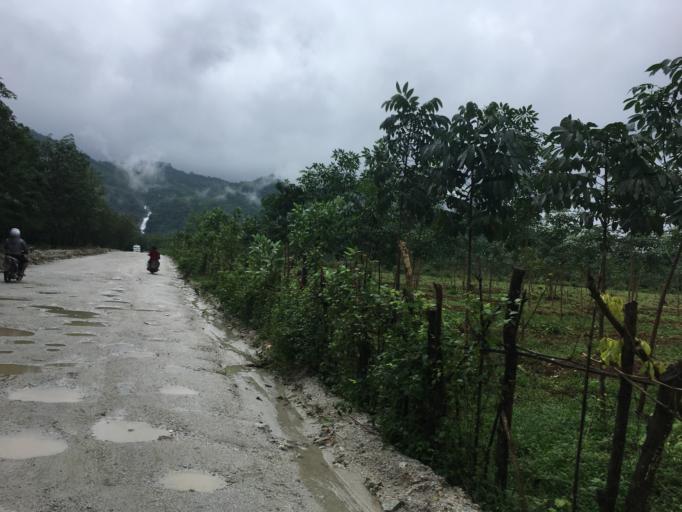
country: MM
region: Mon
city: Martaban
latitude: 16.6706
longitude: 97.5215
